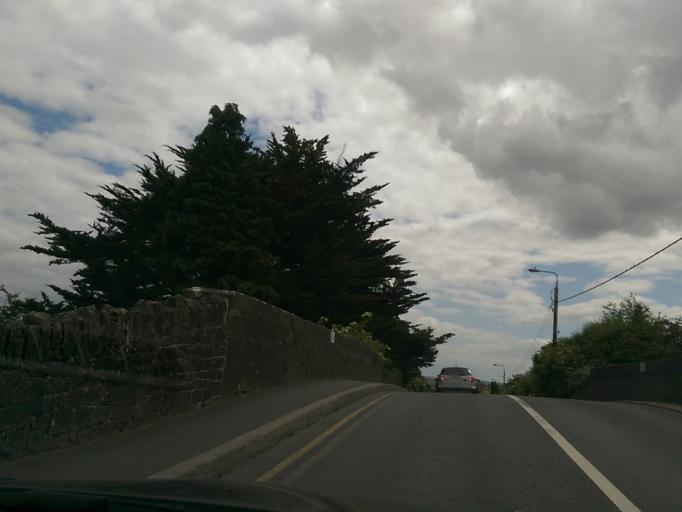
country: IE
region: Munster
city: Thurles
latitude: 52.6824
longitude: -7.8211
